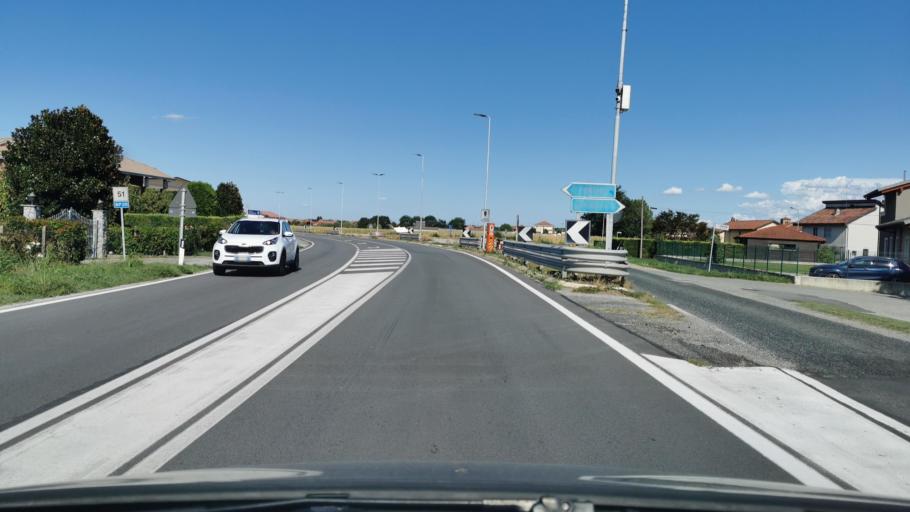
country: IT
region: Piedmont
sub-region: Provincia di Cuneo
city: Genola
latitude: 44.5879
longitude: 7.6534
